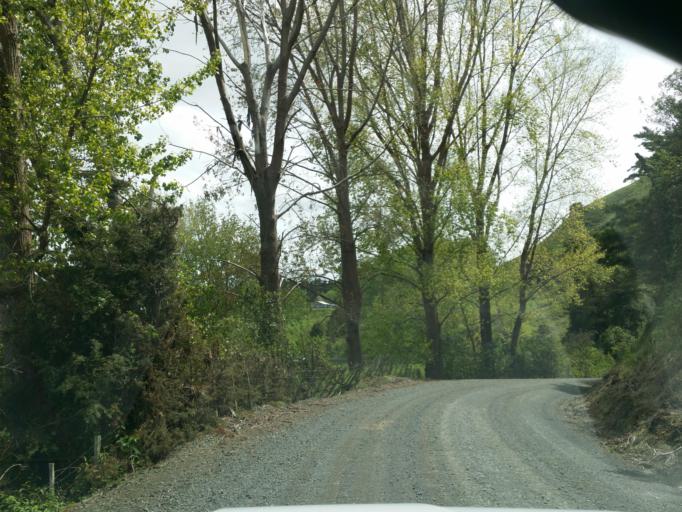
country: NZ
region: Northland
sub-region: Whangarei
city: Maungatapere
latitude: -35.8998
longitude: 174.0965
